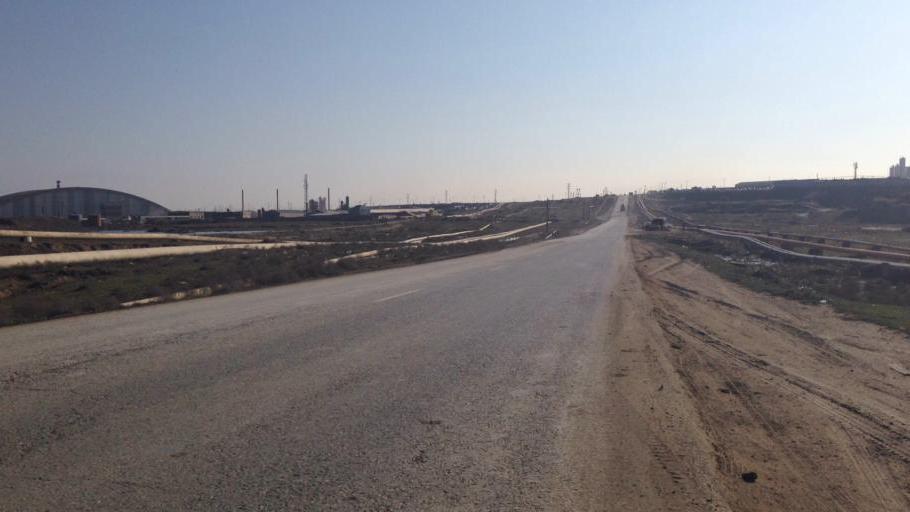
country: AZ
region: Abseron
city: Digah
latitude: 40.4693
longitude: 49.8855
